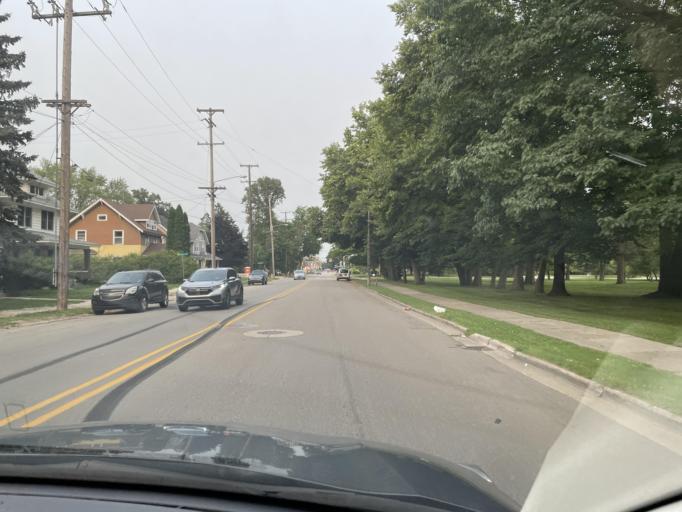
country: US
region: Michigan
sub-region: Kent County
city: Grand Rapids
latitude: 42.9639
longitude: -85.7013
